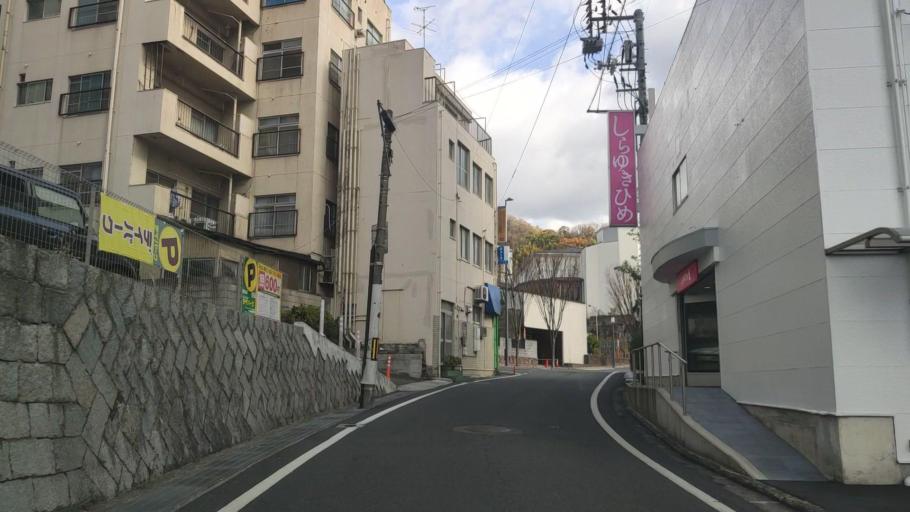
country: JP
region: Ehime
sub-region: Shikoku-chuo Shi
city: Matsuyama
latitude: 33.8544
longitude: 132.7842
